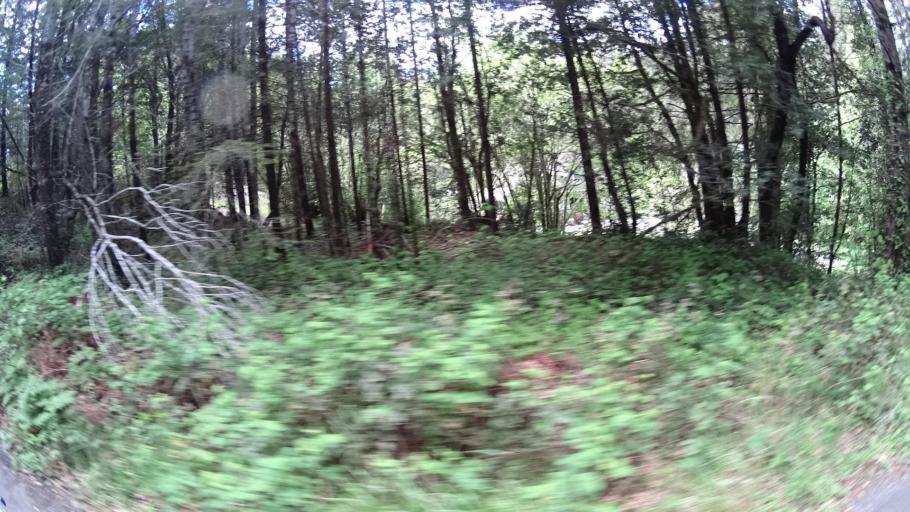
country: US
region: California
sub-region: Humboldt County
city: Blue Lake
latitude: 40.7748
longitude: -123.8771
